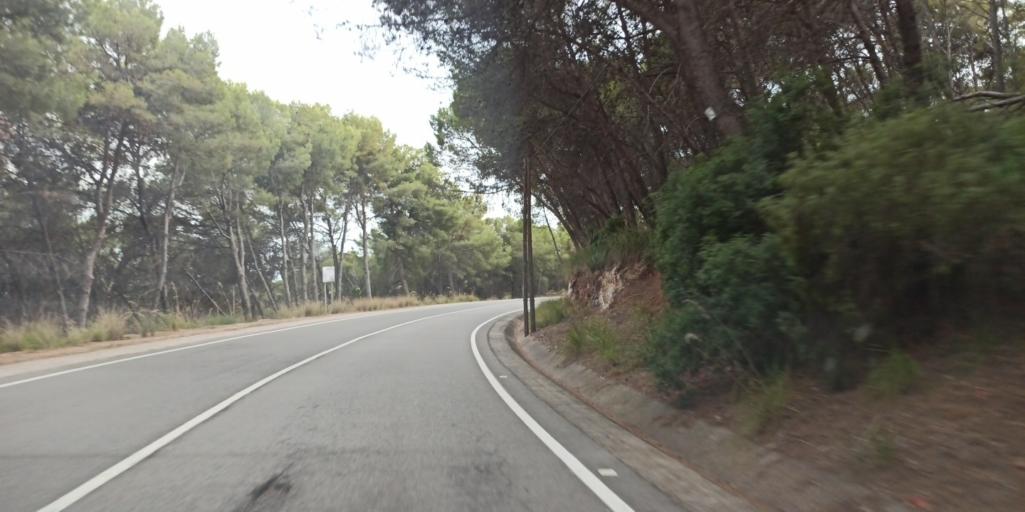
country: ES
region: Catalonia
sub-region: Provincia de Barcelona
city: Castelldefels
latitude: 41.2925
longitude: 1.9740
